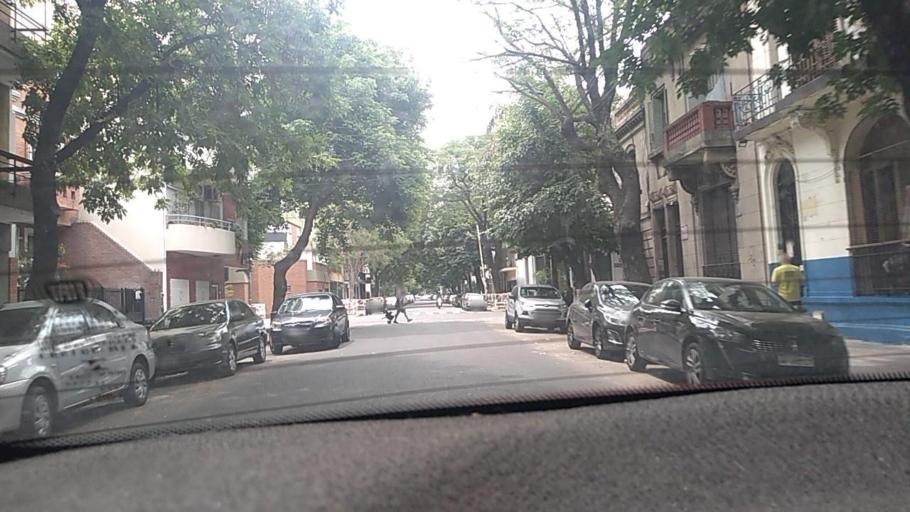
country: AR
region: Buenos Aires F.D.
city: Villa Santa Rita
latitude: -34.6347
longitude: -58.4759
